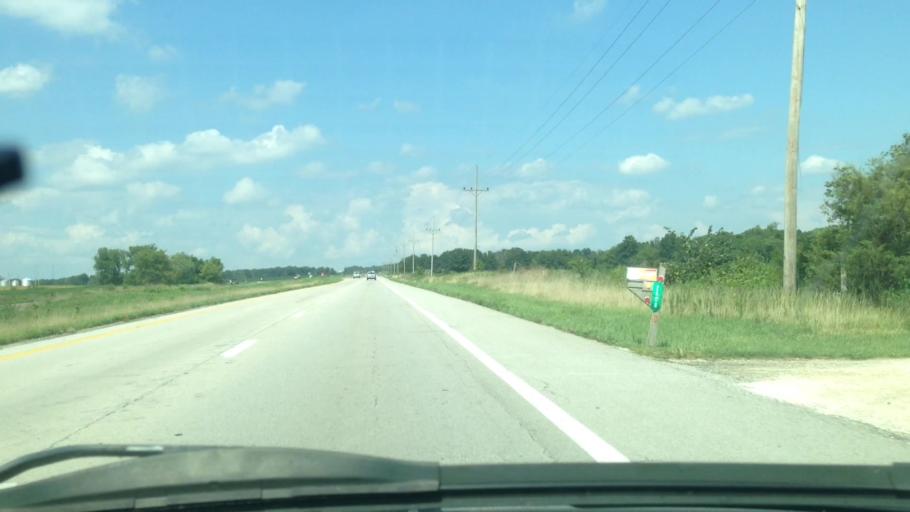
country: US
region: Missouri
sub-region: Lincoln County
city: Troy
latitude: 39.0943
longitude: -90.9670
